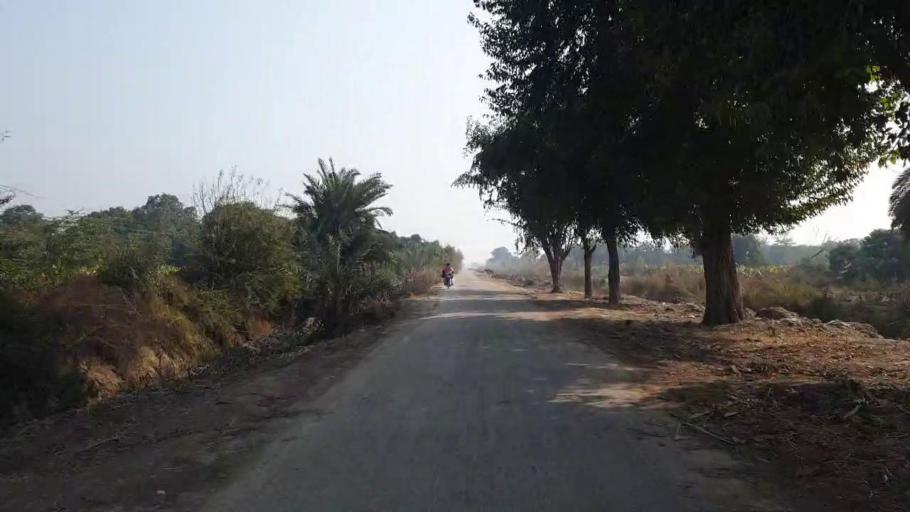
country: PK
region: Sindh
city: Hala
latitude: 25.9596
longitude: 68.4032
